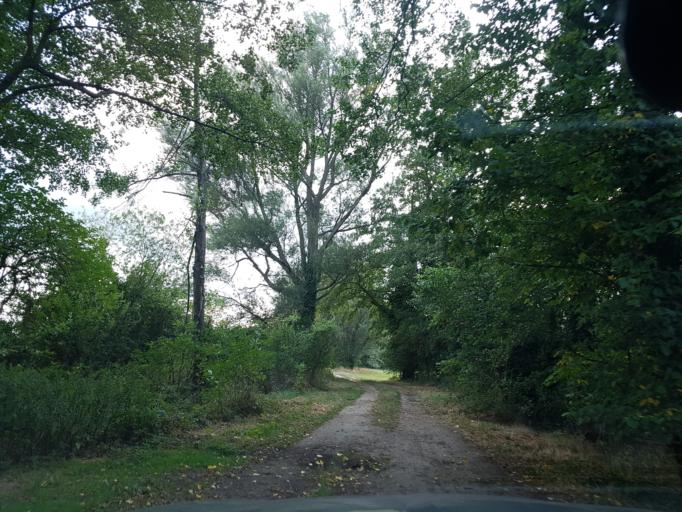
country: DE
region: Brandenburg
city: Herzberg
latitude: 51.6692
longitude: 13.2913
